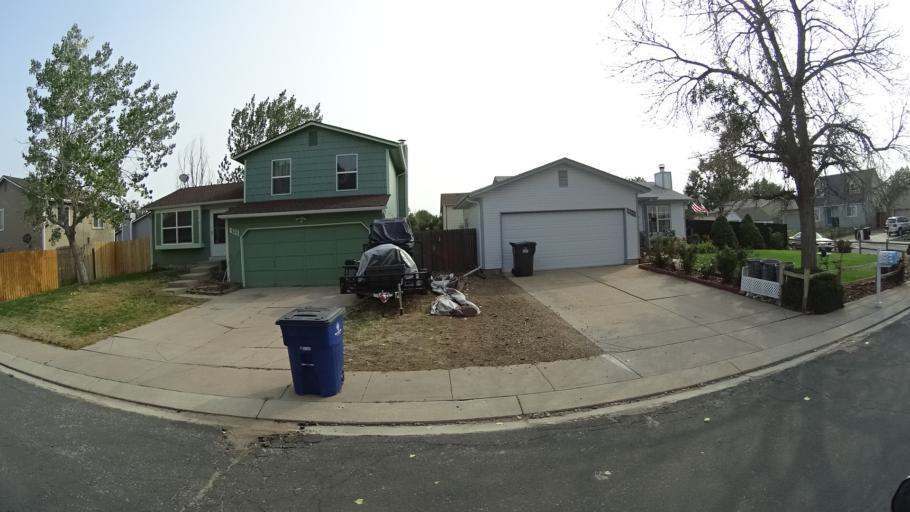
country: US
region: Colorado
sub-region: El Paso County
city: Stratmoor
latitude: 38.8071
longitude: -104.7464
